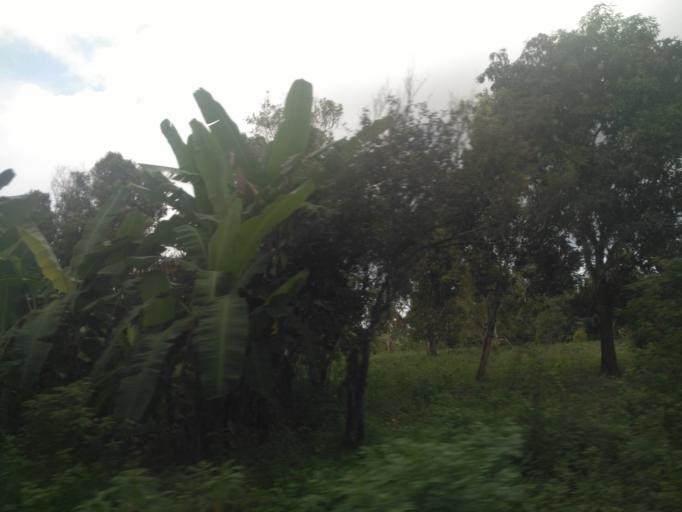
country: TZ
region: Zanzibar Central/South
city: Koani
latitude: -6.1075
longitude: 39.2854
